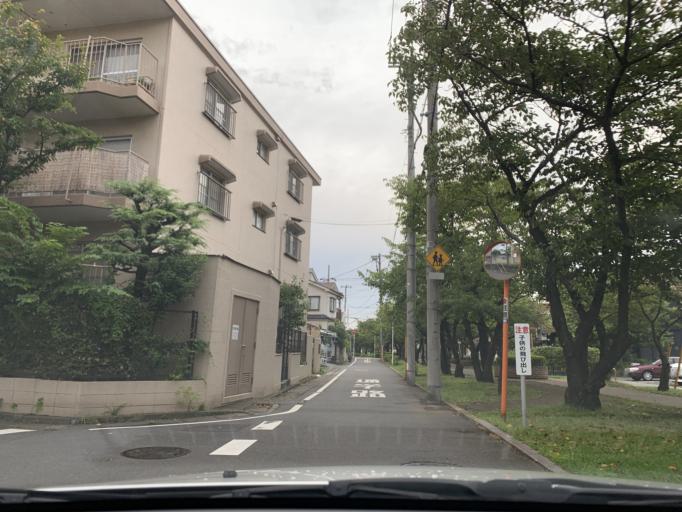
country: JP
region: Tokyo
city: Urayasu
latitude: 35.6793
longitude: 139.9285
